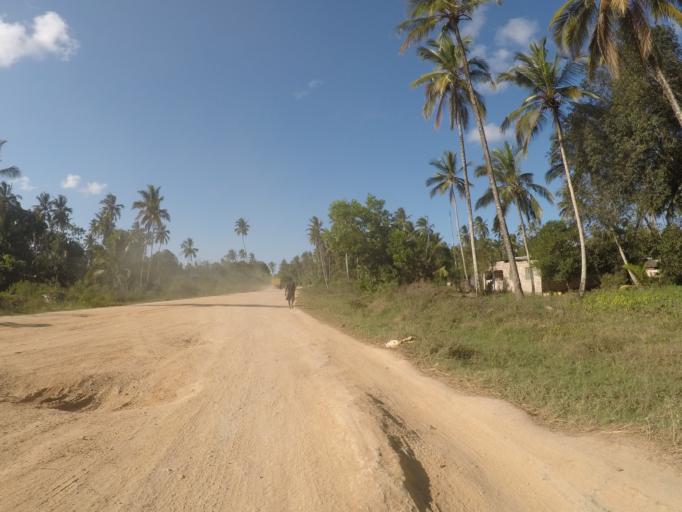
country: TZ
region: Zanzibar Central/South
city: Koani
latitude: -6.1740
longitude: 39.2844
